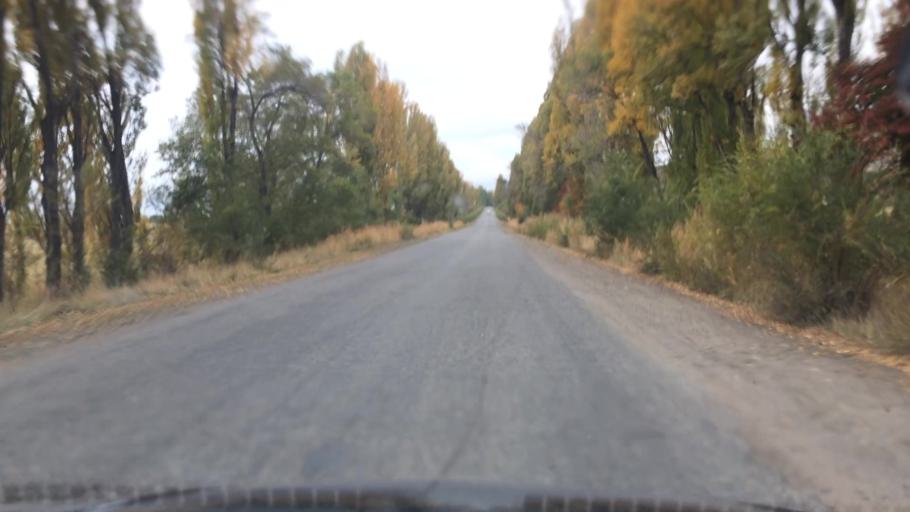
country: KG
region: Ysyk-Koel
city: Pokrovka
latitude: 42.7386
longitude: 77.8918
